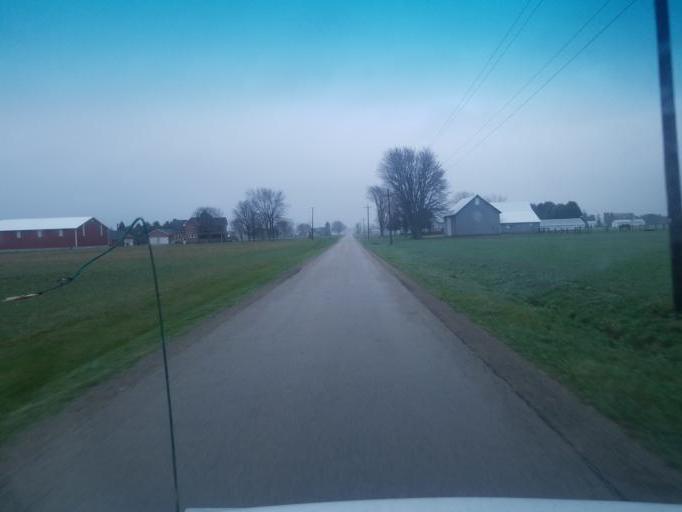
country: US
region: Ohio
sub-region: Fulton County
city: Archbold
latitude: 41.4232
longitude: -84.2477
